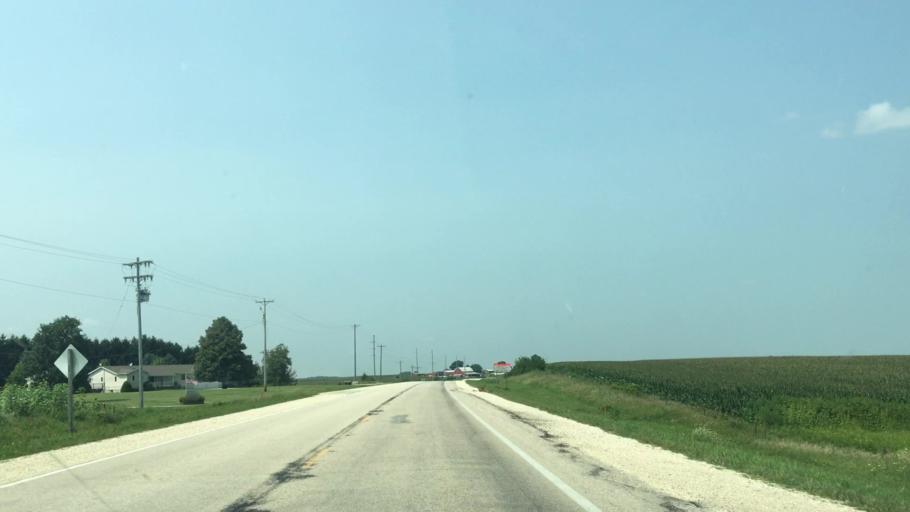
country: US
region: Iowa
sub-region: Fayette County
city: West Union
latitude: 42.9729
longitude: -91.8186
